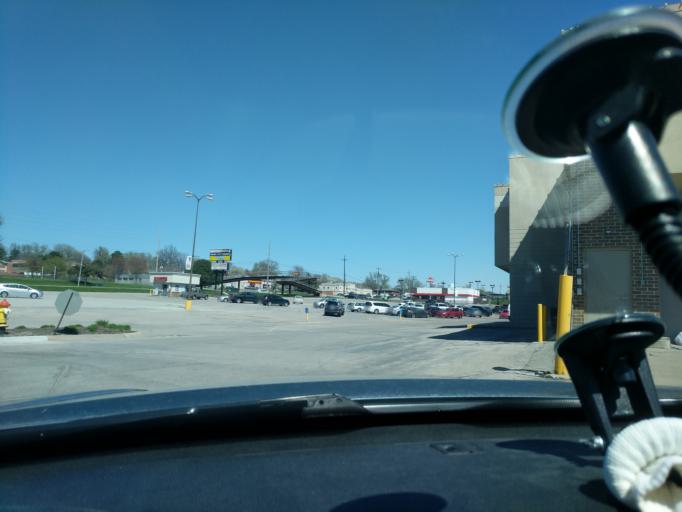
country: US
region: Nebraska
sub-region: Douglas County
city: Ralston
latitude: 41.2334
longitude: -96.0473
